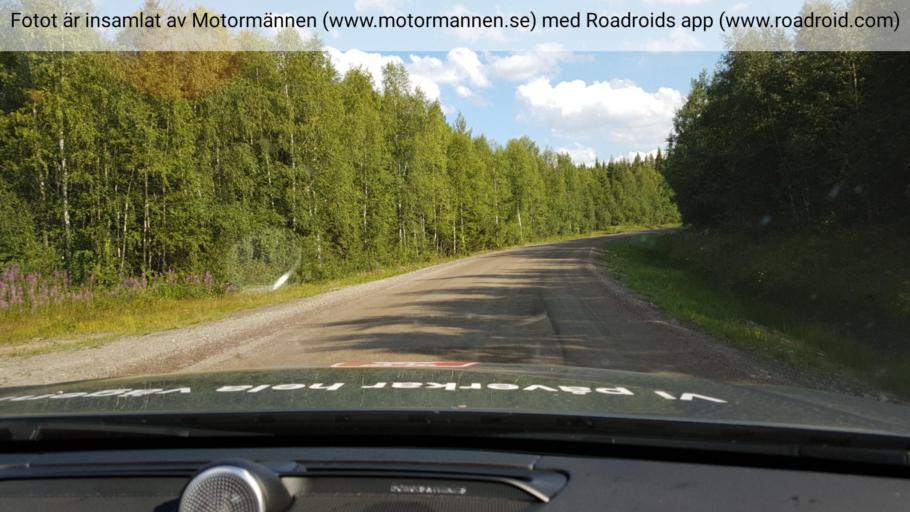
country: SE
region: Jaemtland
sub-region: Stroemsunds Kommun
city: Stroemsund
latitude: 64.0088
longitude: 15.9649
